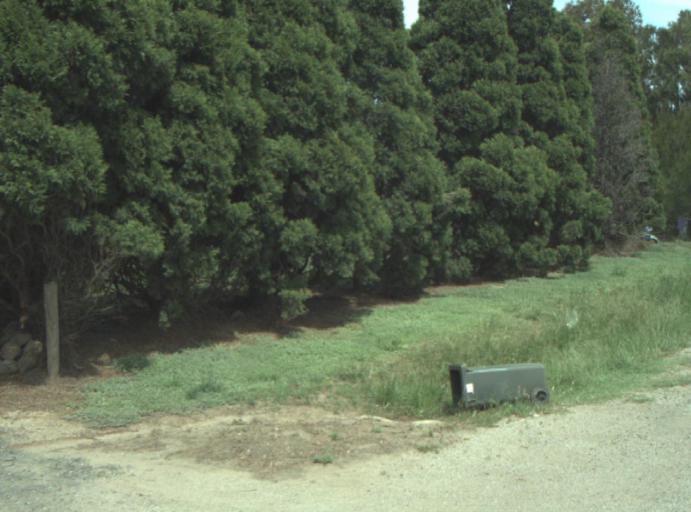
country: AU
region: Victoria
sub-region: Greater Geelong
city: Lara
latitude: -38.0259
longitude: 144.3644
